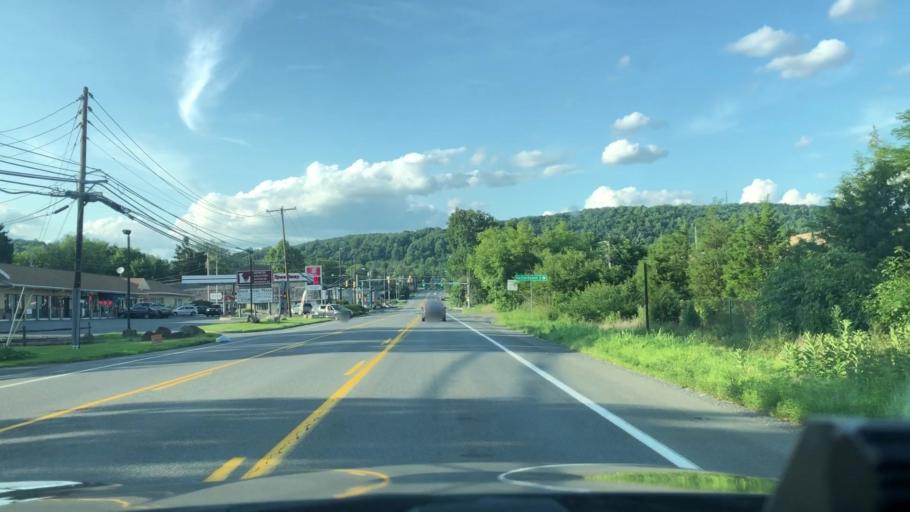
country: US
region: Pennsylvania
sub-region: Lehigh County
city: Fountain Hill
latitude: 40.5806
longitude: -75.3883
